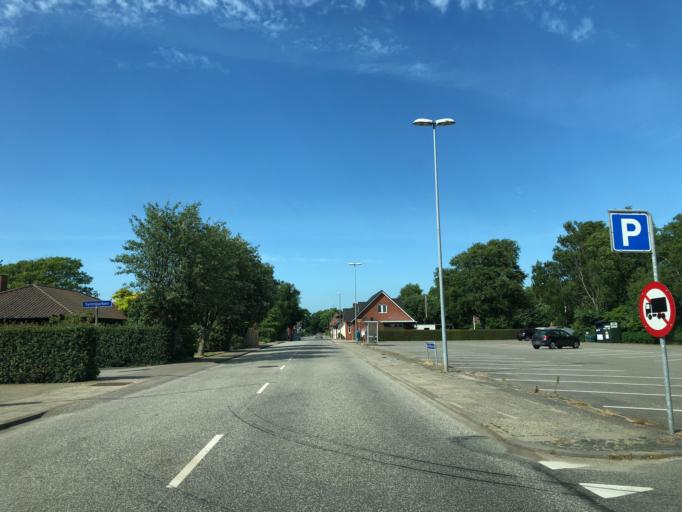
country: DK
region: Central Jutland
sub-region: Herning Kommune
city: Snejbjerg
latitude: 56.1295
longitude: 8.8890
